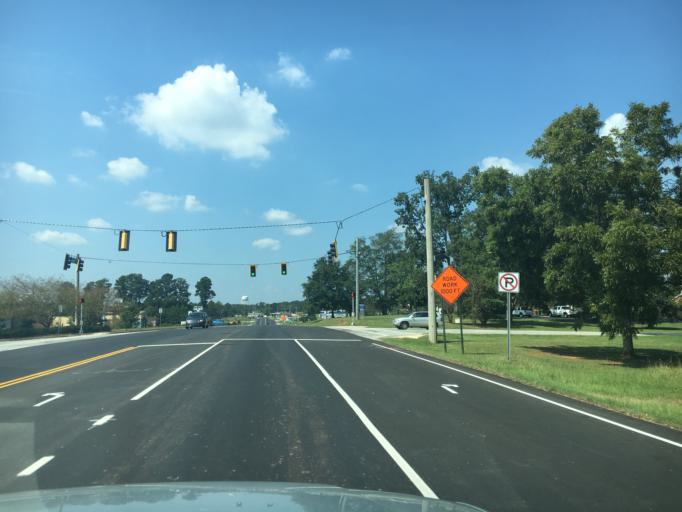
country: US
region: Georgia
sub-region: Hart County
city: Hartwell
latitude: 34.3510
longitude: -82.9025
